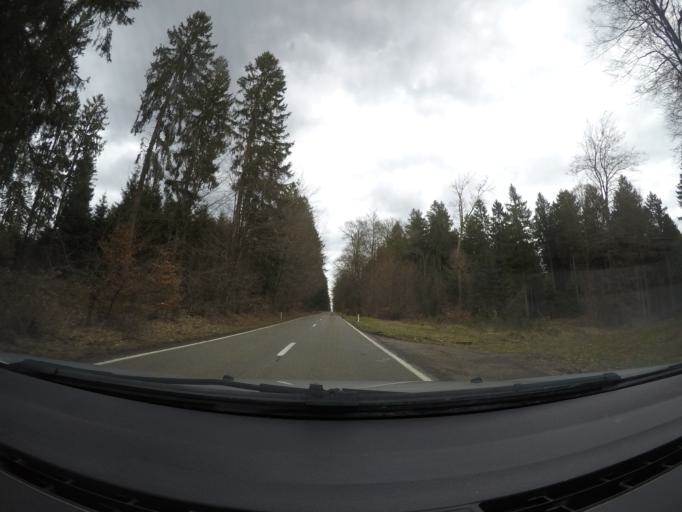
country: BE
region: Wallonia
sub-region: Province du Luxembourg
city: Leglise
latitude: 49.7632
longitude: 5.4844
